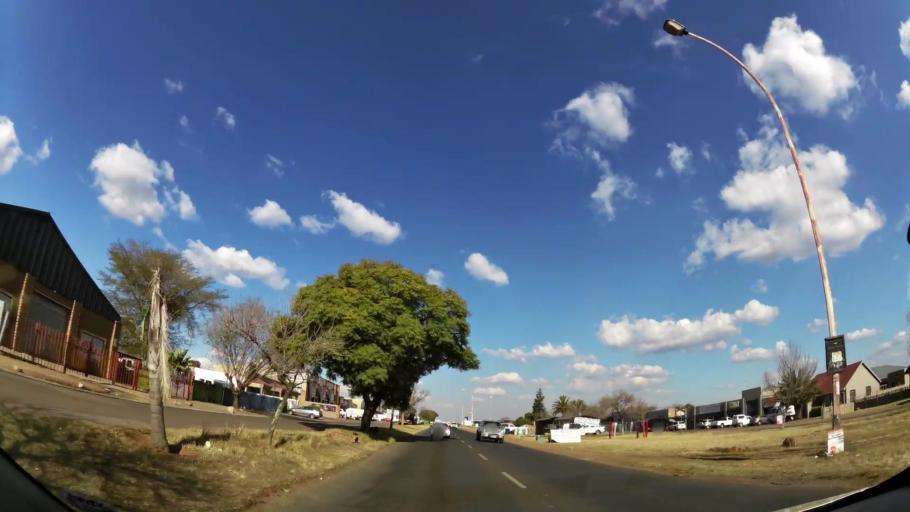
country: ZA
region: Mpumalanga
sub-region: Nkangala District Municipality
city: Witbank
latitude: -25.8912
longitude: 29.2258
